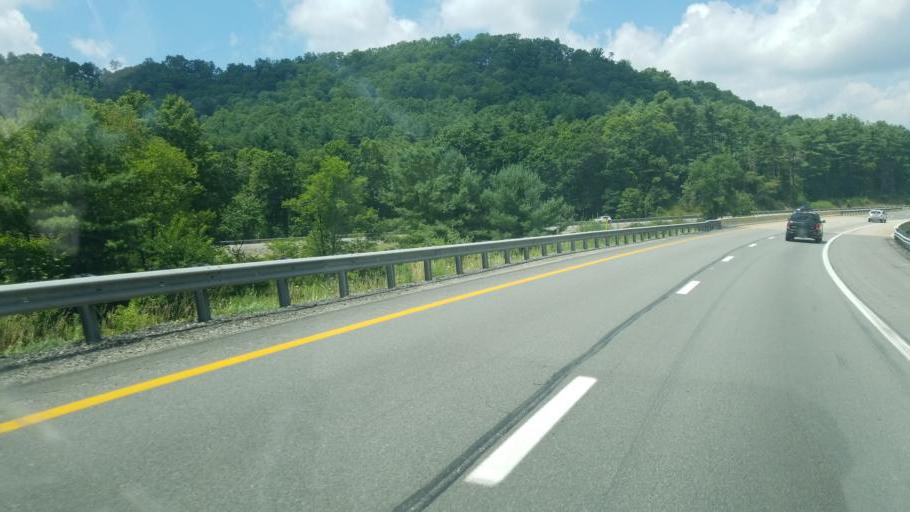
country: US
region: West Virginia
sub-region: Raleigh County
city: Beaver
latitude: 37.7099
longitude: -81.1505
